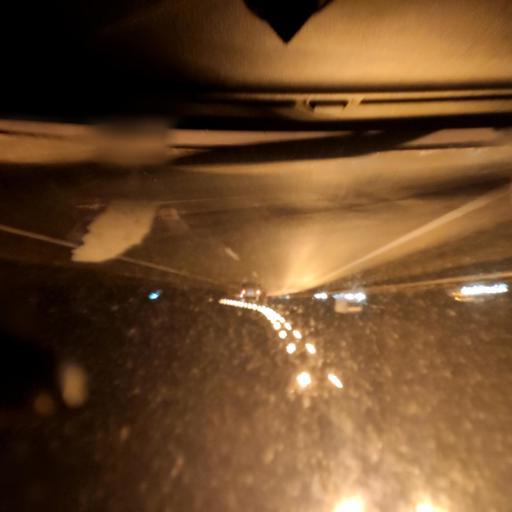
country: RU
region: Tatarstan
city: Osinovo
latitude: 55.7591
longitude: 48.8132
